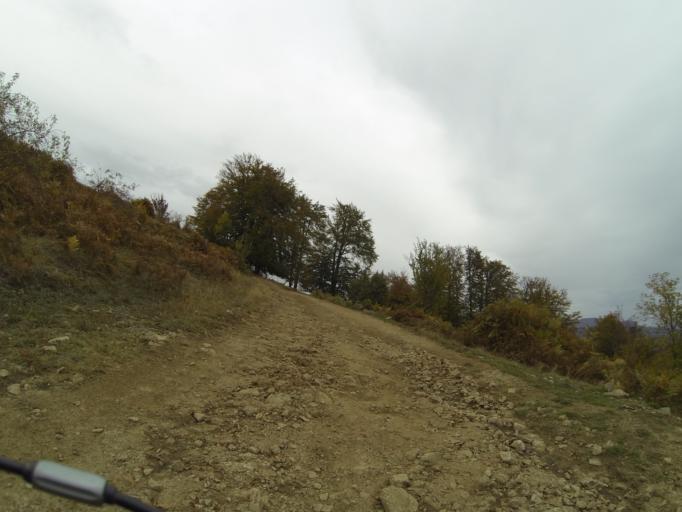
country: RO
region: Gorj
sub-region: Comuna Pades
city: Closani
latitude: 45.0911
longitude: 22.8389
